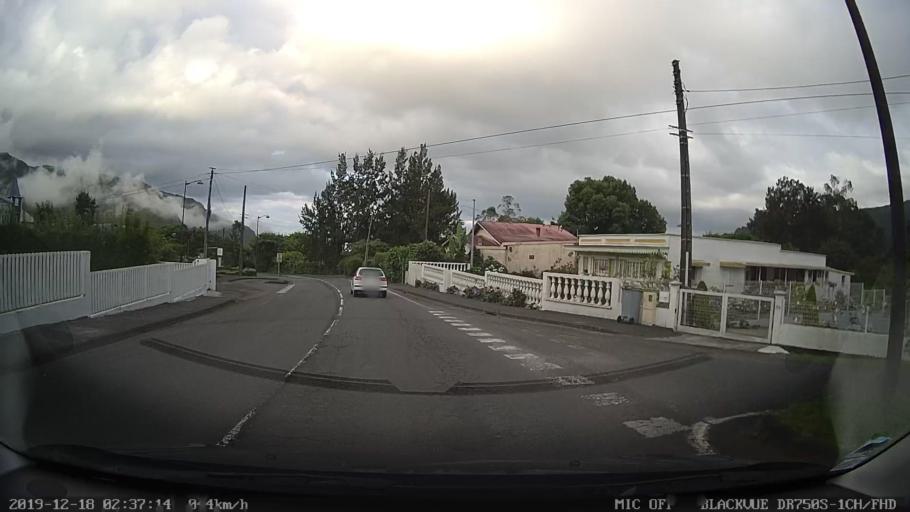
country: RE
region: Reunion
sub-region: Reunion
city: Saint-Benoit
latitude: -21.1383
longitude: 55.6239
